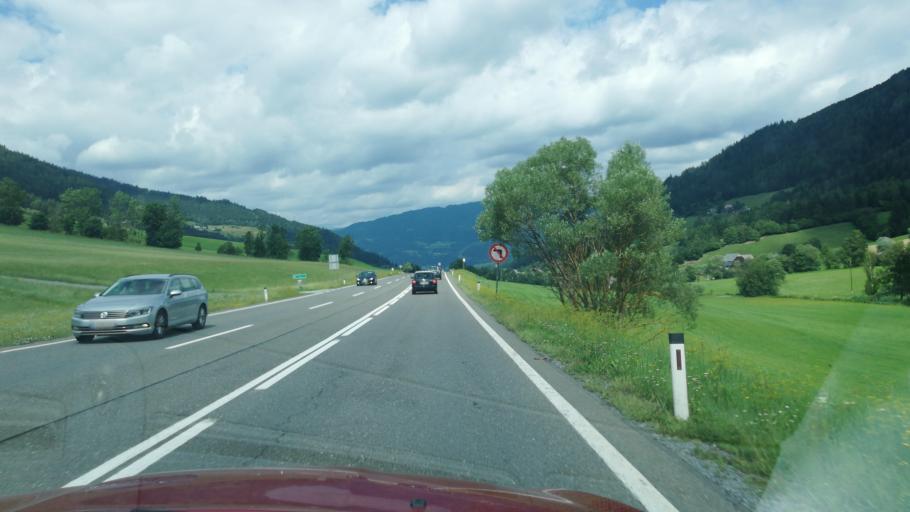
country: AT
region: Styria
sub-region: Politischer Bezirk Murau
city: Perchau am Sattel
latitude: 47.1176
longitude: 14.4517
